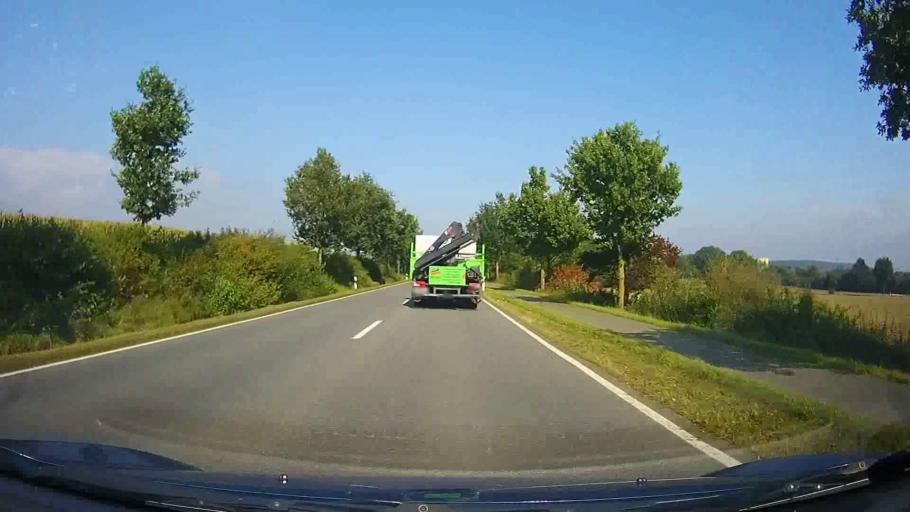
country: DE
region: Lower Saxony
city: Moringen
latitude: 51.6812
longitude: 9.8590
